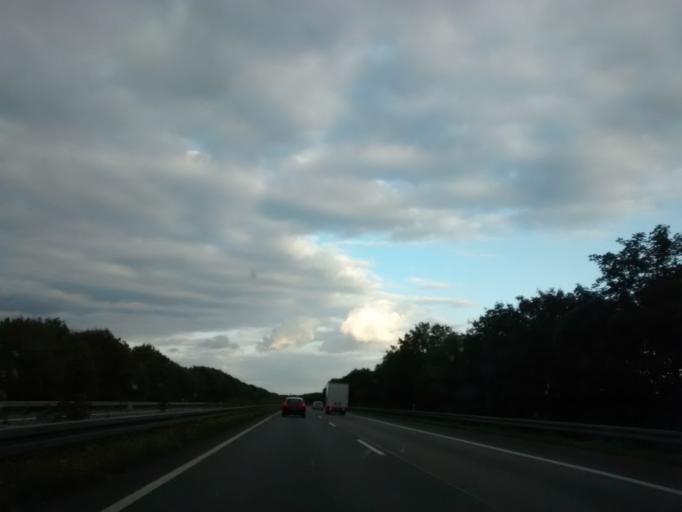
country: DE
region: North Rhine-Westphalia
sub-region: Regierungsbezirk Munster
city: Horstel
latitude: 52.2892
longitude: 7.5634
